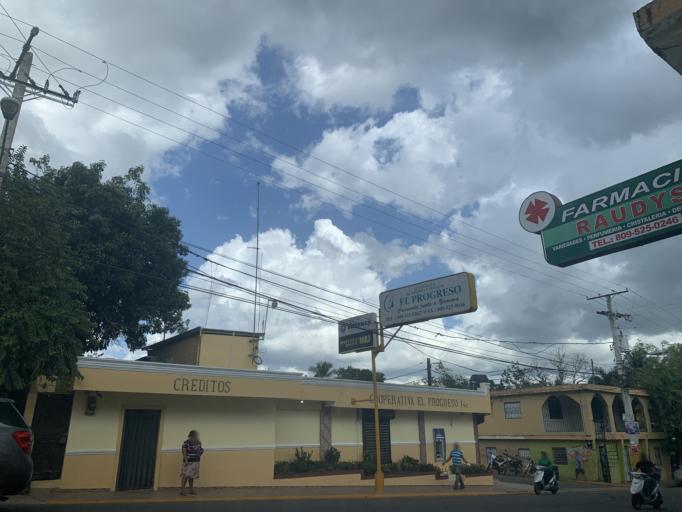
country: DO
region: Monte Plata
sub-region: Yamasa
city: Yamasa
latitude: 18.7665
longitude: -70.0227
